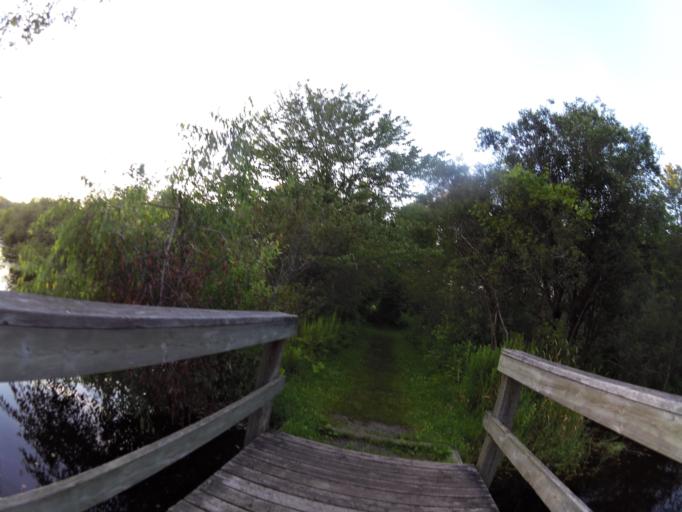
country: CA
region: Ontario
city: Ottawa
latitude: 45.4070
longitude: -75.5657
